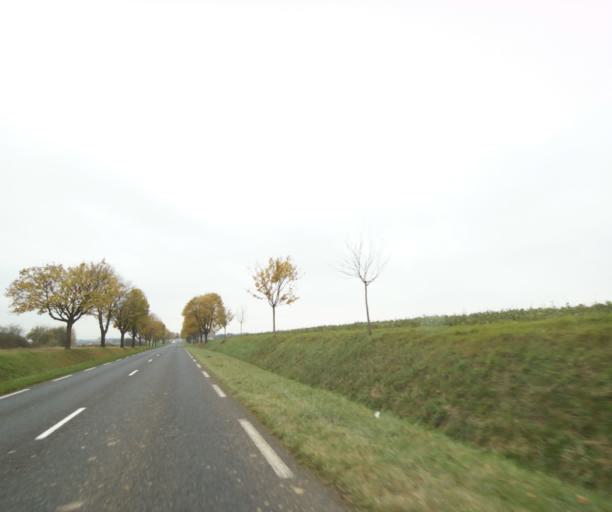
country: FR
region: Lorraine
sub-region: Departement de Meurthe-et-Moselle
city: Briey
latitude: 49.2617
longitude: 5.9507
